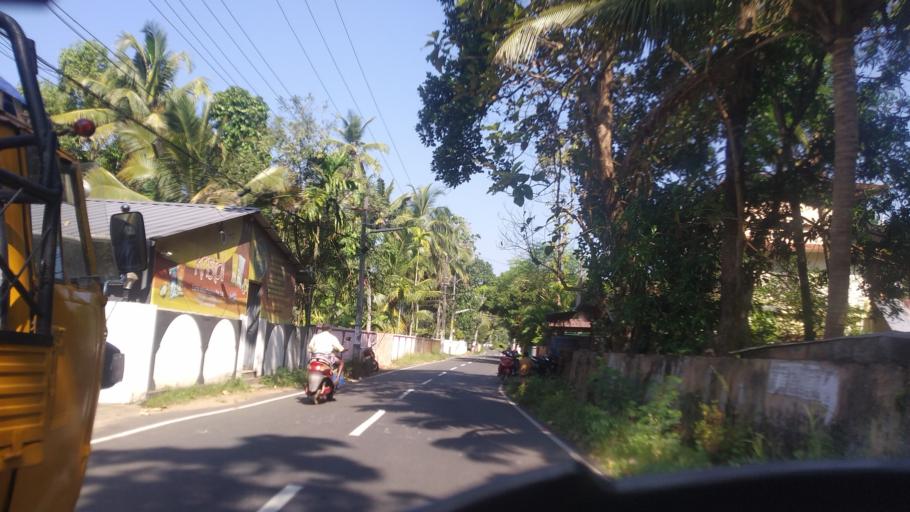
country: IN
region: Kerala
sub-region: Ernakulam
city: Elur
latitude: 10.1148
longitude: 76.2478
